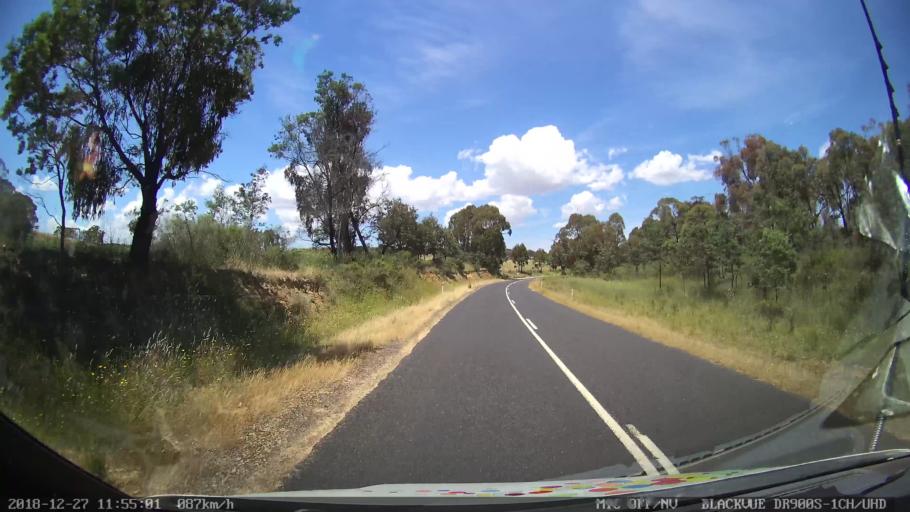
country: AU
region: New South Wales
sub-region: Blayney
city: Blayney
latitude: -33.6823
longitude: 149.4009
